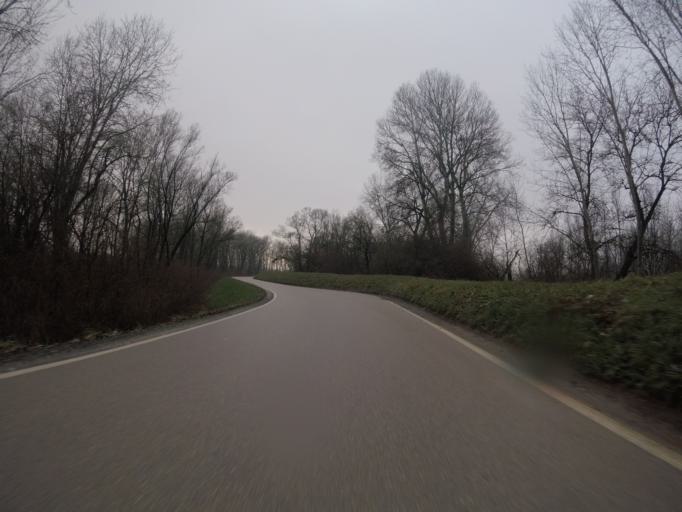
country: HR
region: Zagrebacka
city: Kuce
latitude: 45.6983
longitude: 16.2145
